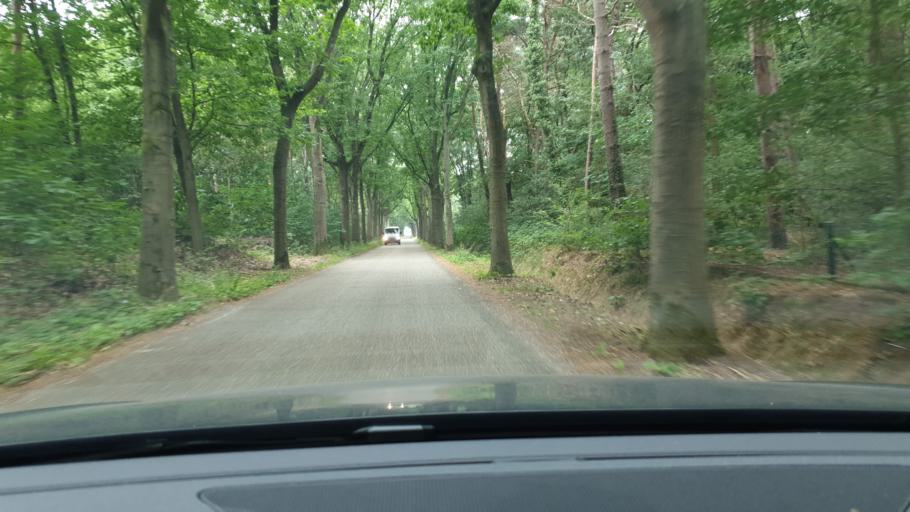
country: NL
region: North Brabant
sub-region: Gemeente Oss
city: Berghem
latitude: 51.7538
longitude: 5.5684
